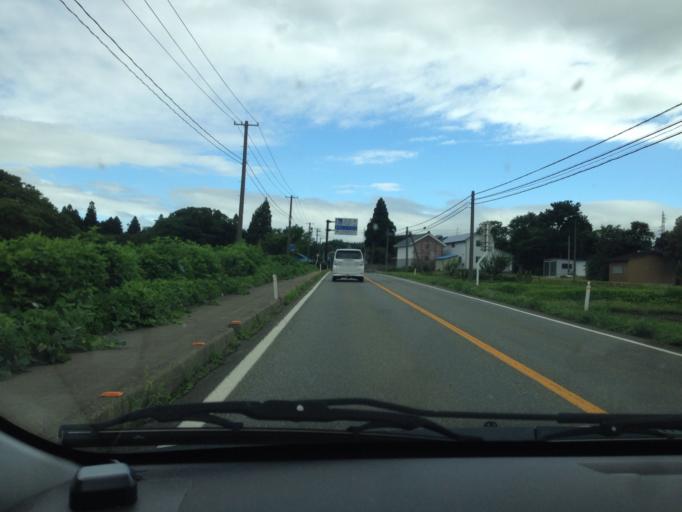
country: JP
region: Fukushima
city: Kitakata
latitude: 37.5666
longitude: 139.9671
